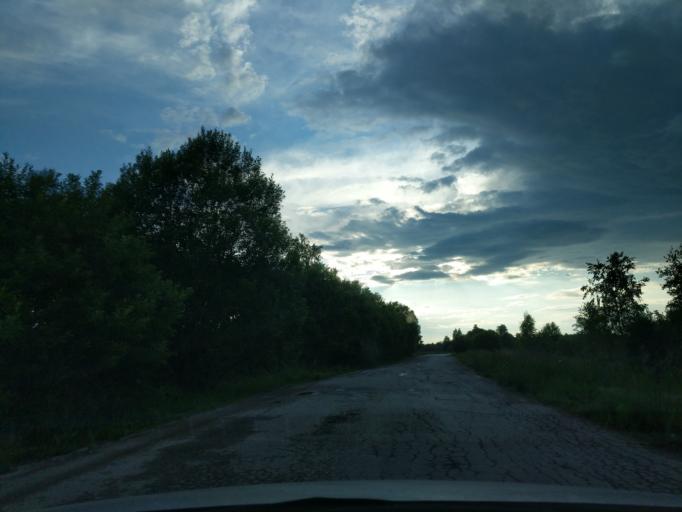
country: RU
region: Kaluga
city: Myatlevo
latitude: 54.8532
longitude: 35.5869
